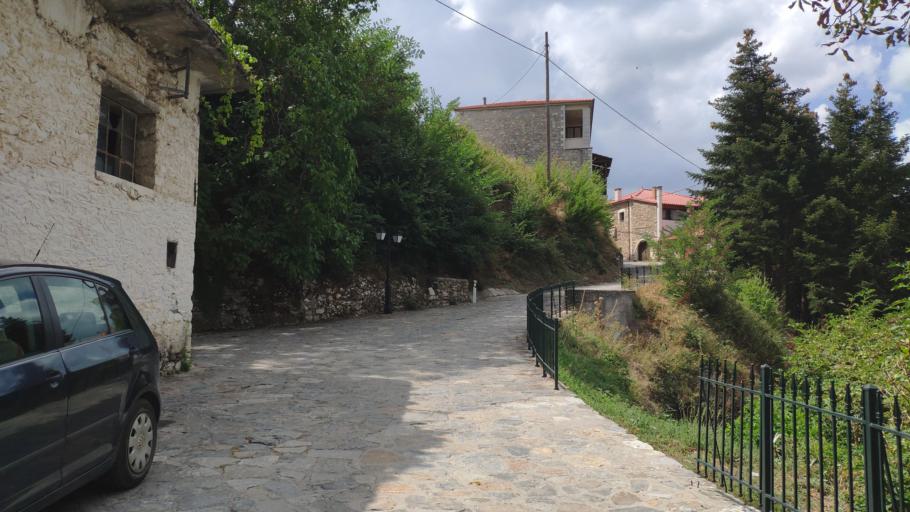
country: GR
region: Peloponnese
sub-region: Nomos Lakonias
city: Kariai
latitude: 37.2439
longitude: 22.5516
